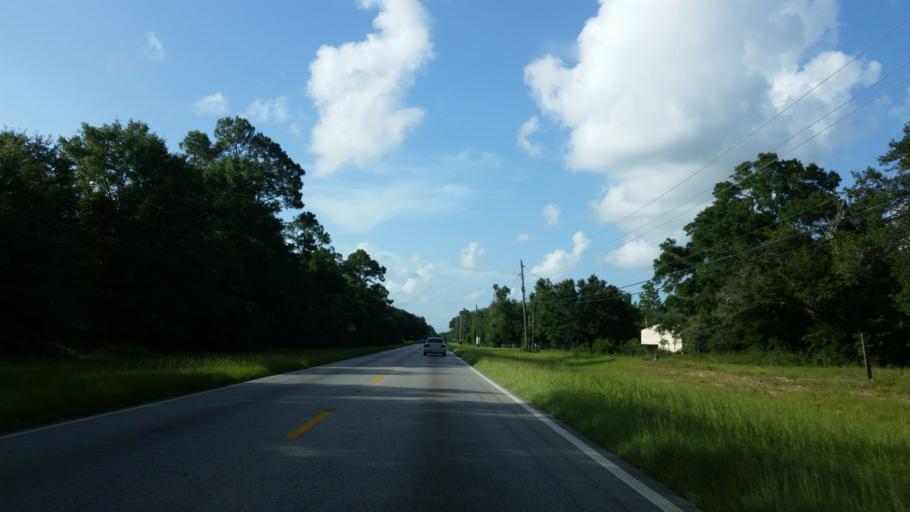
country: US
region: Florida
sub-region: Santa Rosa County
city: Bagdad
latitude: 30.5762
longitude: -87.0313
